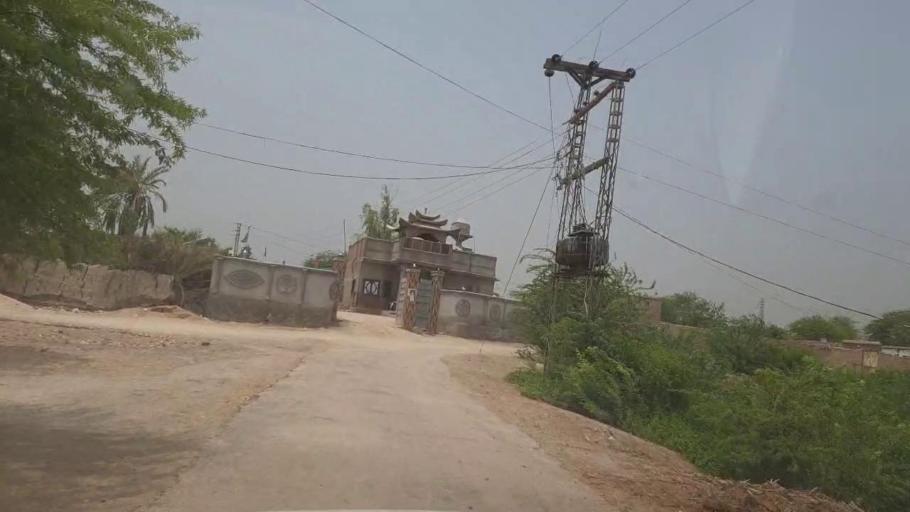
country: PK
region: Sindh
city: Kot Diji
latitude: 27.4407
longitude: 68.6447
